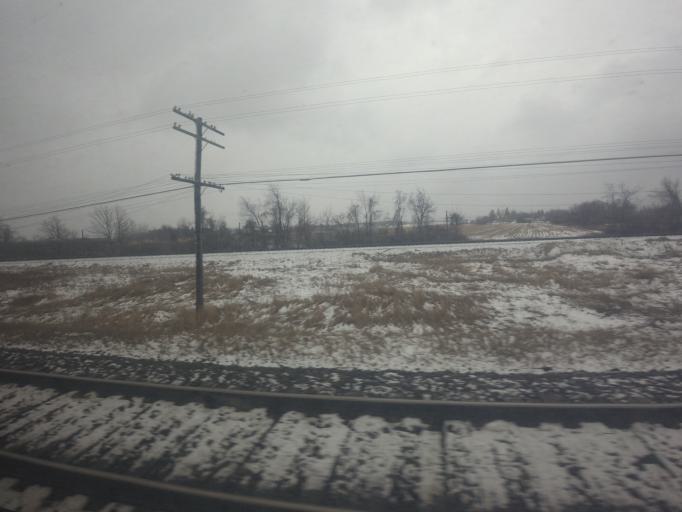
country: CA
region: Ontario
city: Quinte West
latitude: 44.0918
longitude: -77.6282
